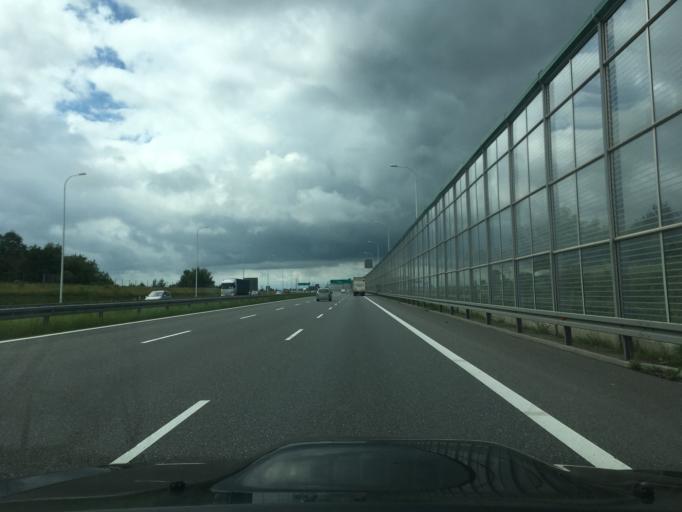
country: PL
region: Lublin Voivodeship
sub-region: Powiat lubelski
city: Jakubowice Murowane
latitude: 51.2982
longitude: 22.6001
